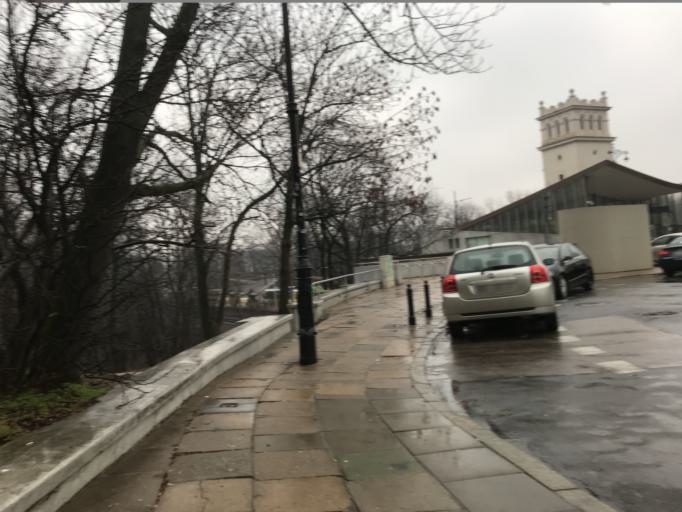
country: PL
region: Masovian Voivodeship
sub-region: Warszawa
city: Srodmiescie
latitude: 52.2334
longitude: 21.0257
